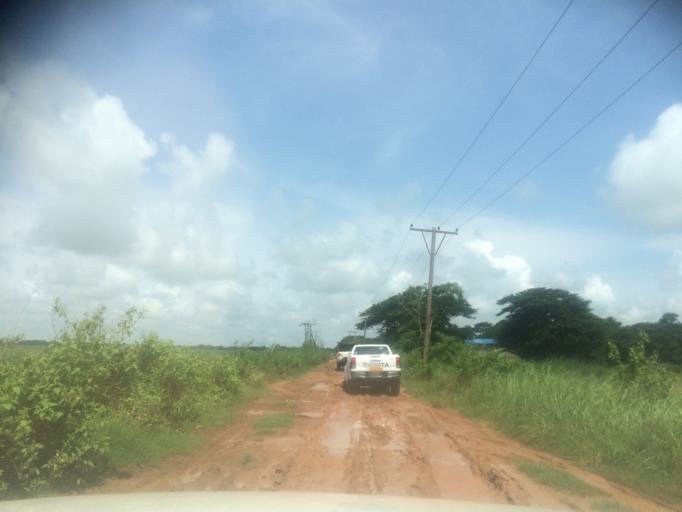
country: MM
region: Bago
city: Tharyarwady
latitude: 17.3175
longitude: 95.8979
